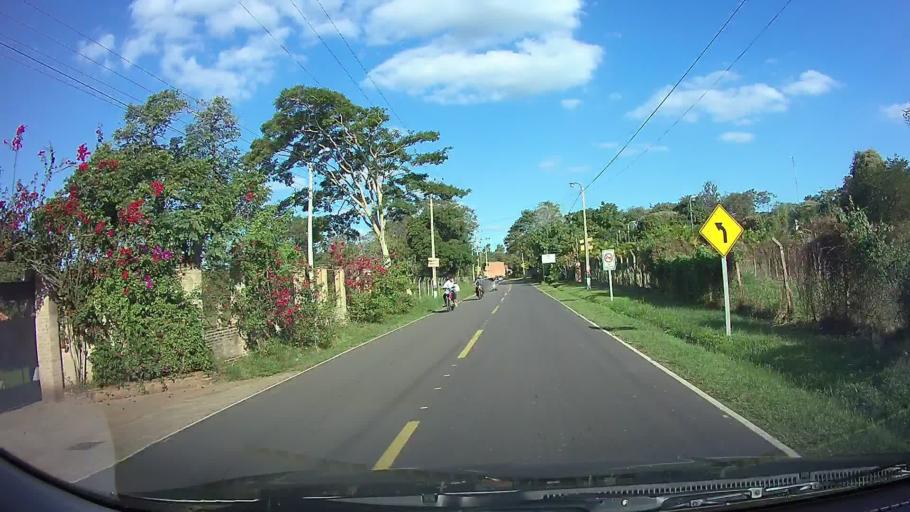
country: PY
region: Central
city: Aregua
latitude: -25.3028
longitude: -57.3893
